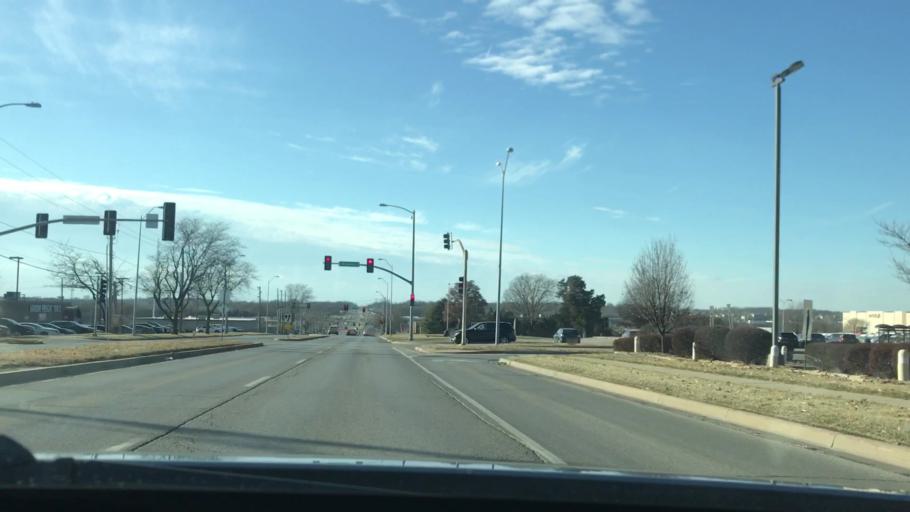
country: US
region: Missouri
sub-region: Clay County
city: Gladstone
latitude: 39.2464
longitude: -94.5826
